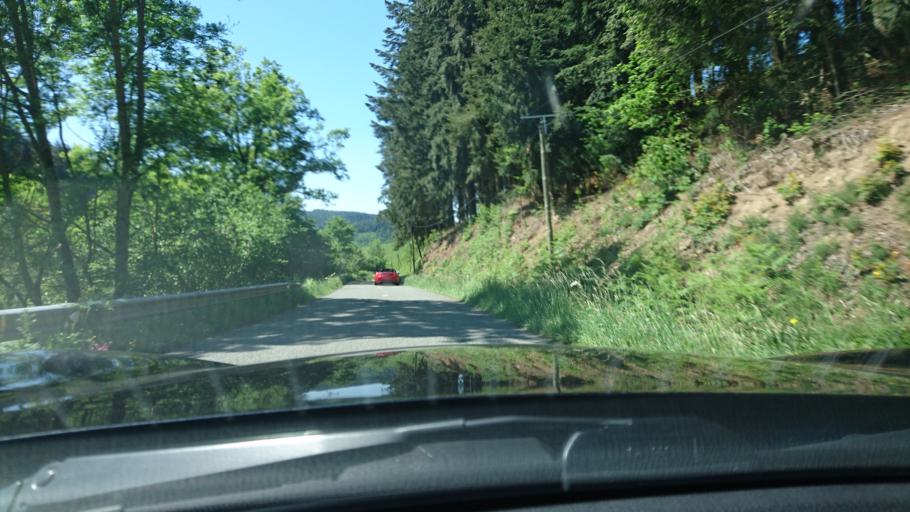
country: FR
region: Rhone-Alpes
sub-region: Departement de la Loire
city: Saint-Just-la-Pendue
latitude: 45.8878
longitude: 4.3030
